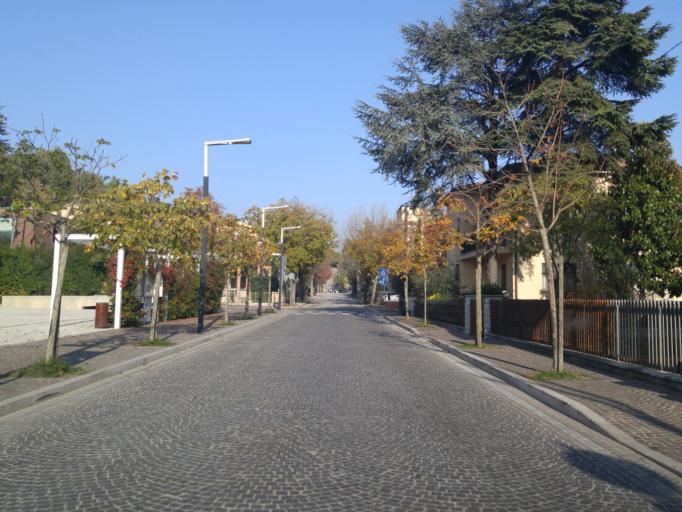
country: IT
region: The Marches
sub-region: Provincia di Pesaro e Urbino
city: Calcinelli
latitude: 43.7518
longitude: 12.9179
